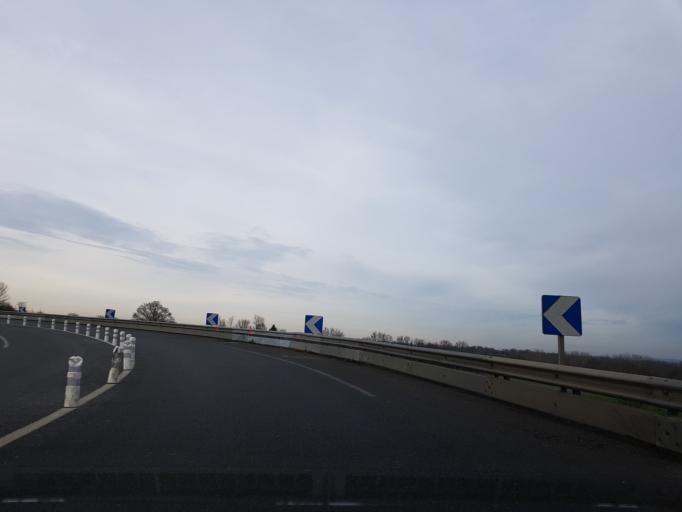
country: FR
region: Auvergne
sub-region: Departement de l'Allier
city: Doyet
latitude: 46.3970
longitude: 2.7169
